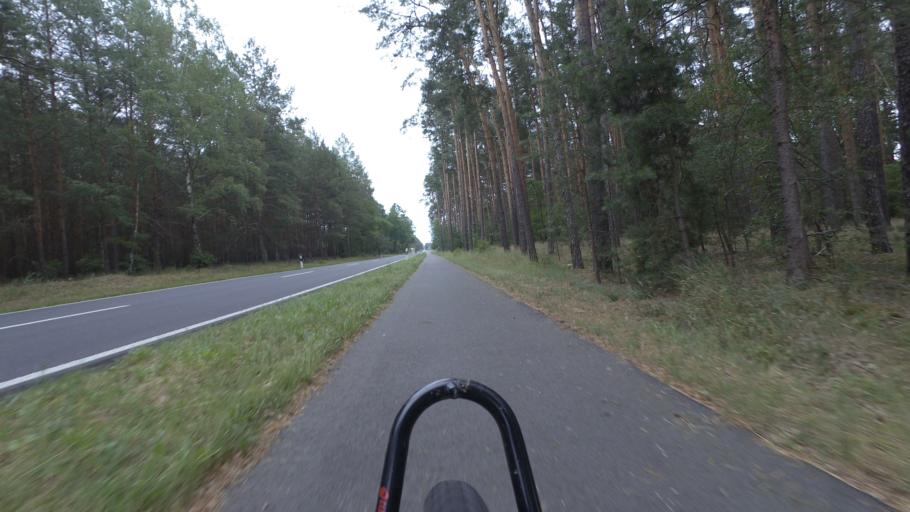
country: DE
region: Brandenburg
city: Sperenberg
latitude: 52.0840
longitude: 13.3044
